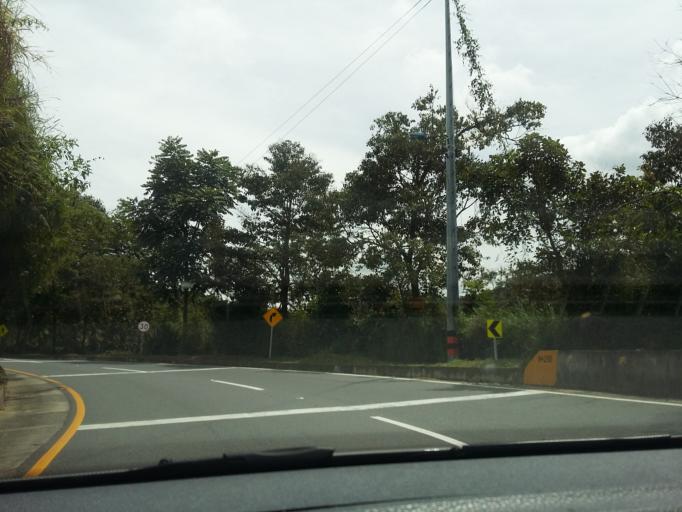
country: CO
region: Santander
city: Bucaramanga
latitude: 7.1096
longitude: -73.0787
